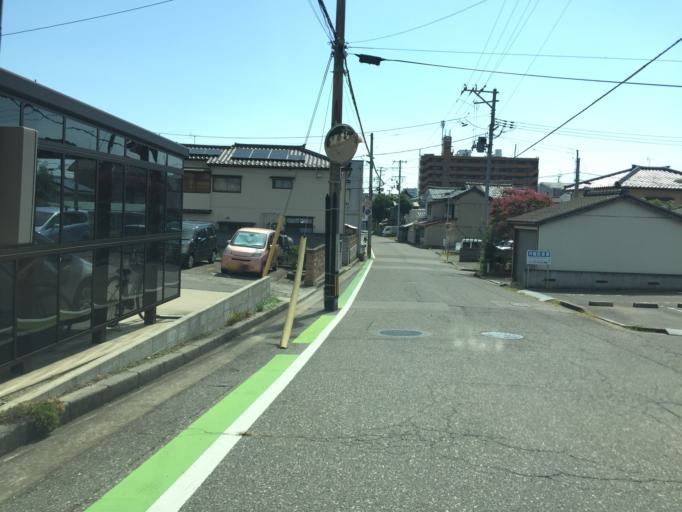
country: JP
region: Niigata
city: Niigata-shi
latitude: 37.9338
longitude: 139.0455
